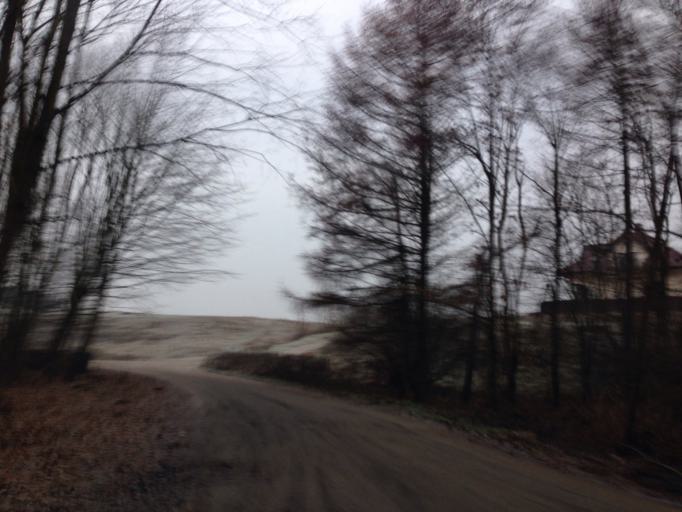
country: PL
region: Kujawsko-Pomorskie
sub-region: Powiat brodnicki
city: Gorzno
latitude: 53.2237
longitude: 19.6500
